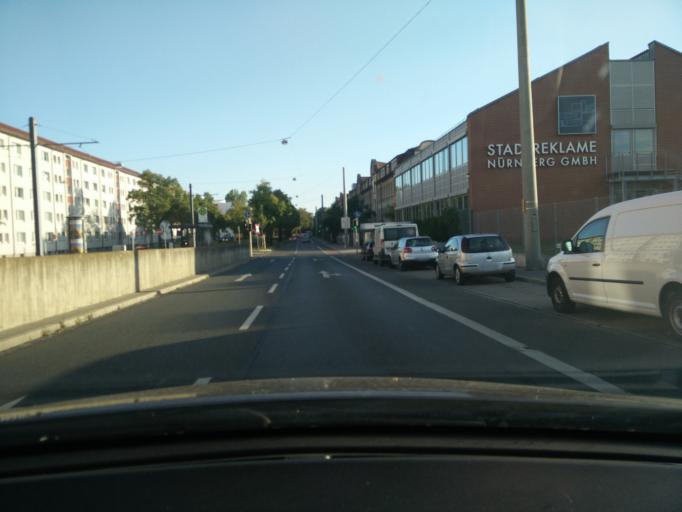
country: DE
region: Bavaria
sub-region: Regierungsbezirk Mittelfranken
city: Nuernberg
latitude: 49.4240
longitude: 11.0852
